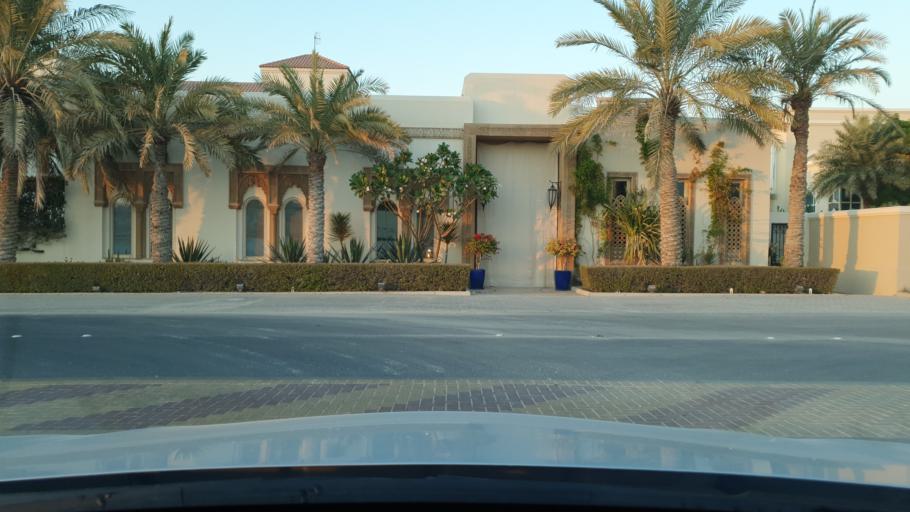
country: BH
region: Northern
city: Ar Rifa'
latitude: 26.1411
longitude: 50.5313
